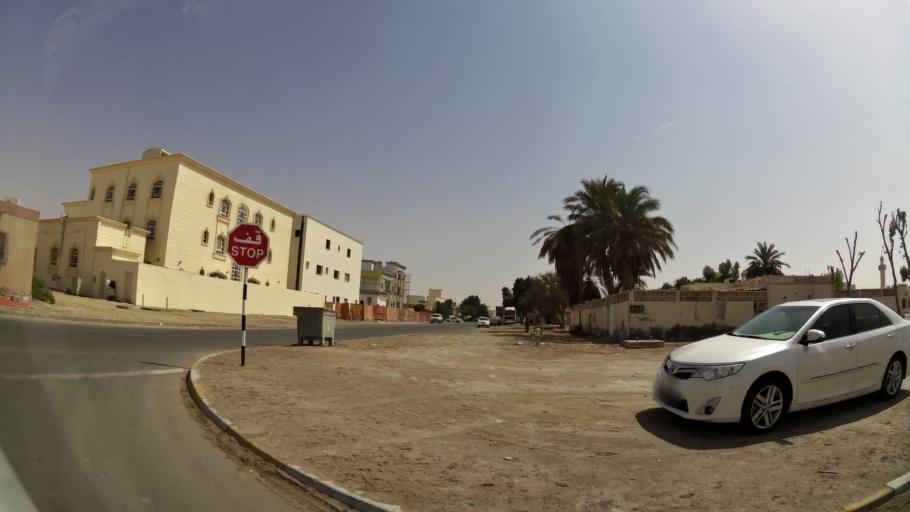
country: AE
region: Abu Dhabi
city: Abu Dhabi
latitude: 24.2918
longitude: 54.6425
